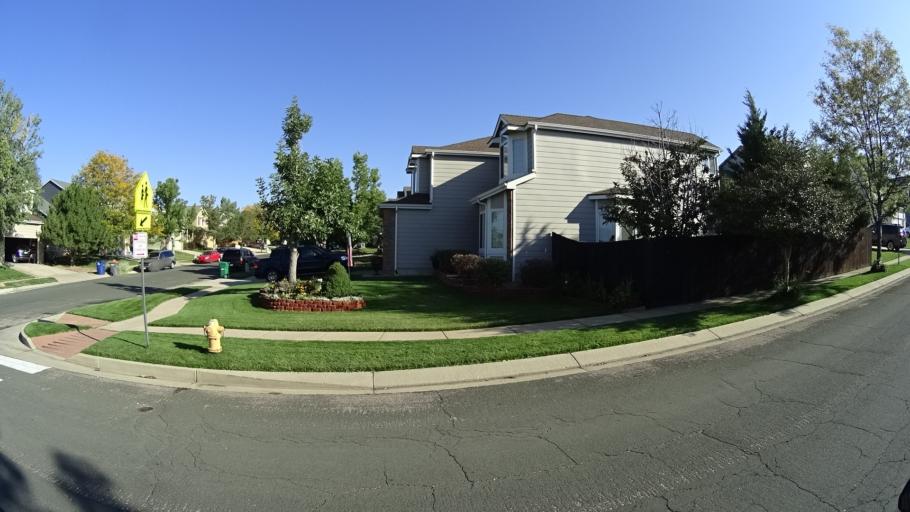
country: US
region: Colorado
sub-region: El Paso County
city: Cimarron Hills
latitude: 38.8789
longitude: -104.6982
